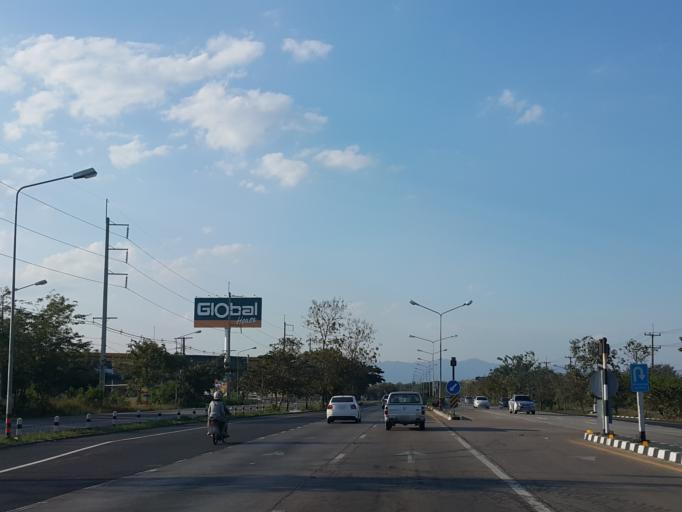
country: TH
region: Lampang
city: Lampang
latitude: 18.2789
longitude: 99.4533
